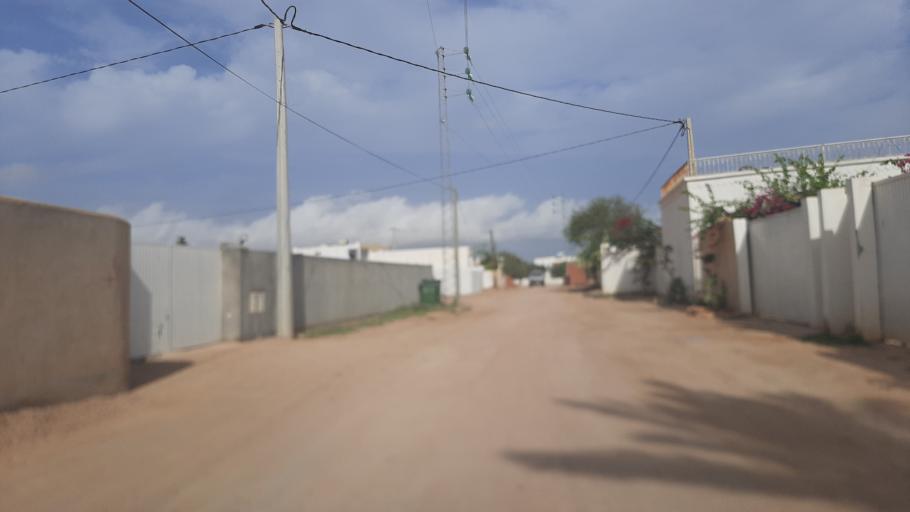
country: TN
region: Madanin
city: Midoun
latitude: 33.7989
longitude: 11.0281
